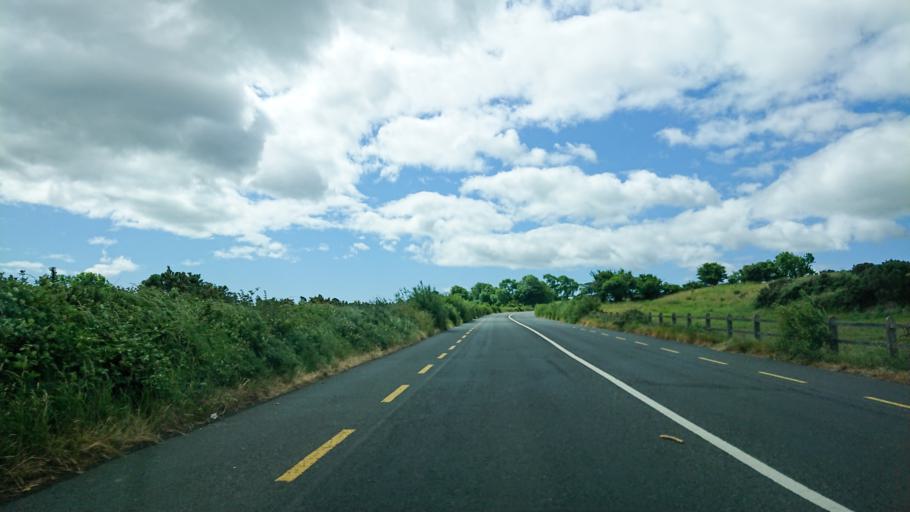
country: IE
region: Munster
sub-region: Waterford
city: Tra Mhor
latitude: 52.2120
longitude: -7.1938
